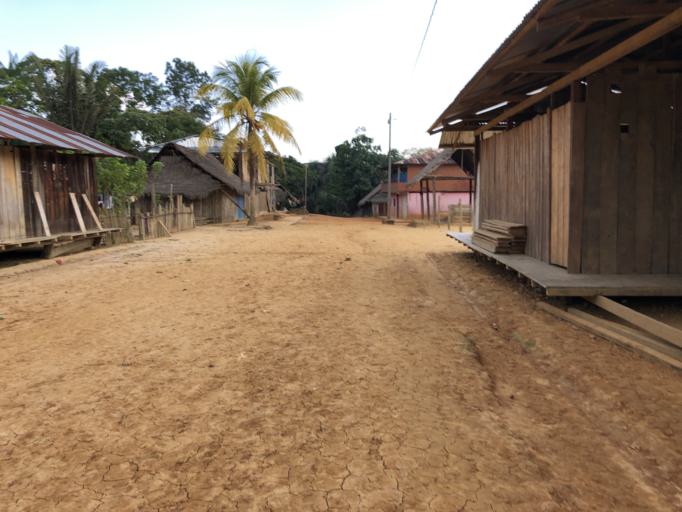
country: PE
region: Loreto
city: Puerto Galilea
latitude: -4.0539
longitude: -77.7614
